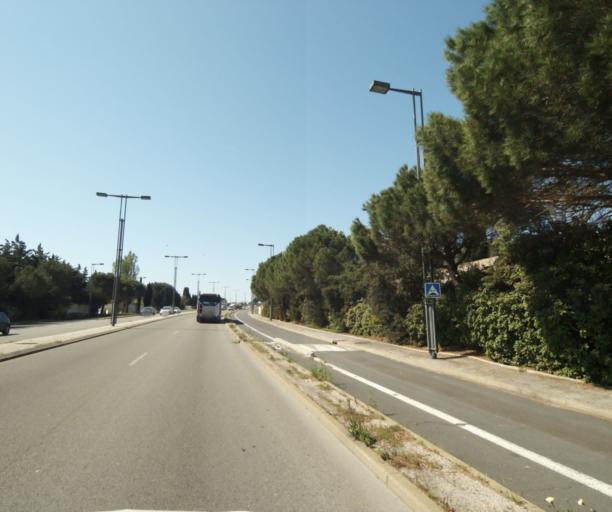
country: FR
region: Languedoc-Roussillon
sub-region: Departement de l'Herault
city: Juvignac
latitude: 43.6284
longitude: 3.8408
